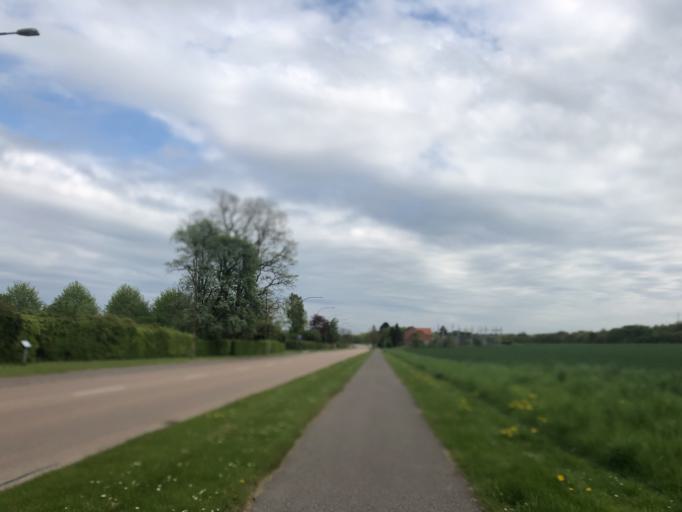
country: DK
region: Zealand
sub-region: Koge Kommune
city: Koge
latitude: 55.4688
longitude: 12.1600
